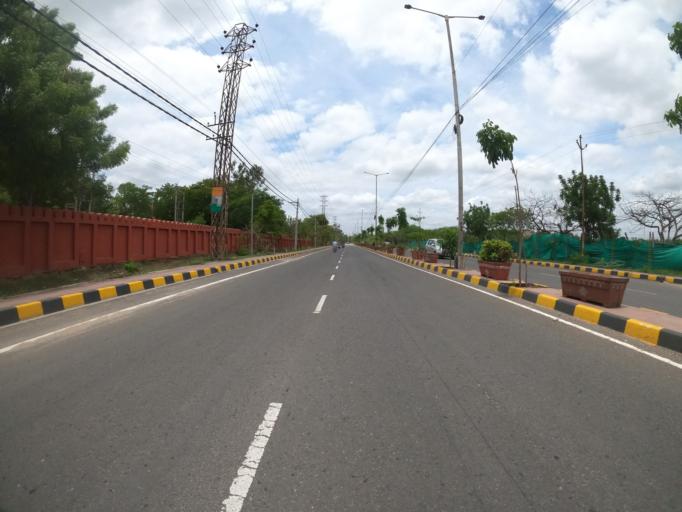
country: IN
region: Telangana
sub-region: Hyderabad
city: Hyderabad
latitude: 17.3740
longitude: 78.4022
